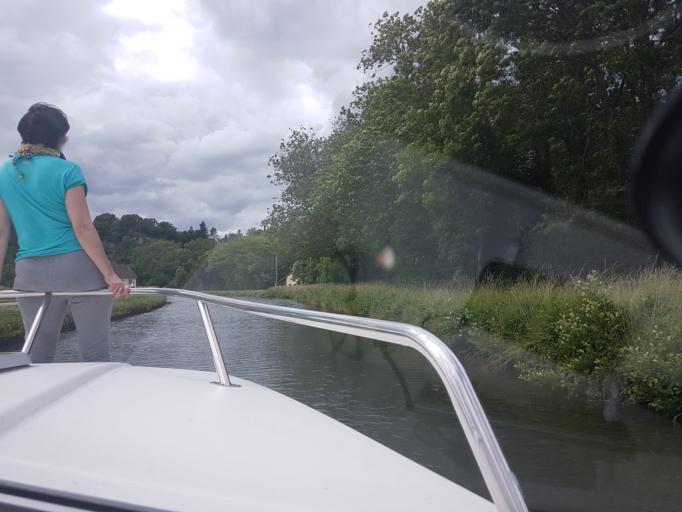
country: FR
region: Bourgogne
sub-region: Departement de l'Yonne
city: Vermenton
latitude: 47.5915
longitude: 3.6396
